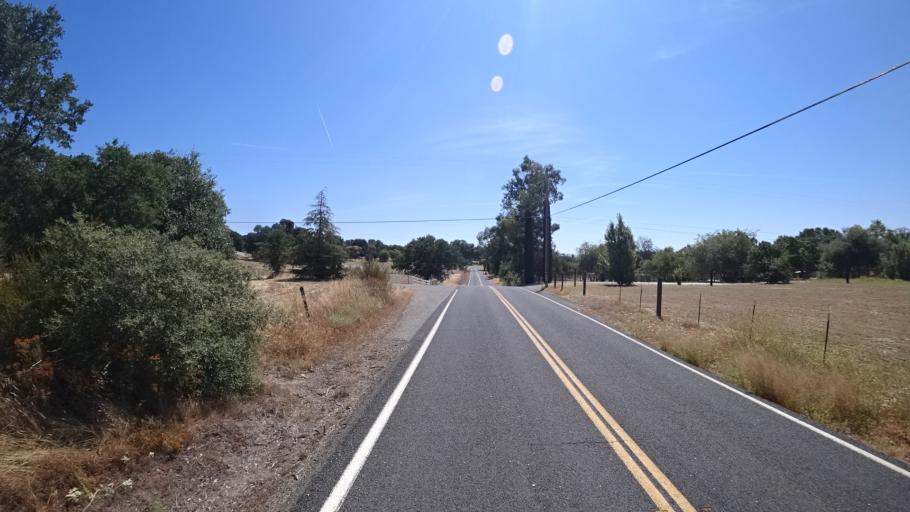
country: US
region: California
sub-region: Calaveras County
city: Rancho Calaveras
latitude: 38.1484
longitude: -120.9361
